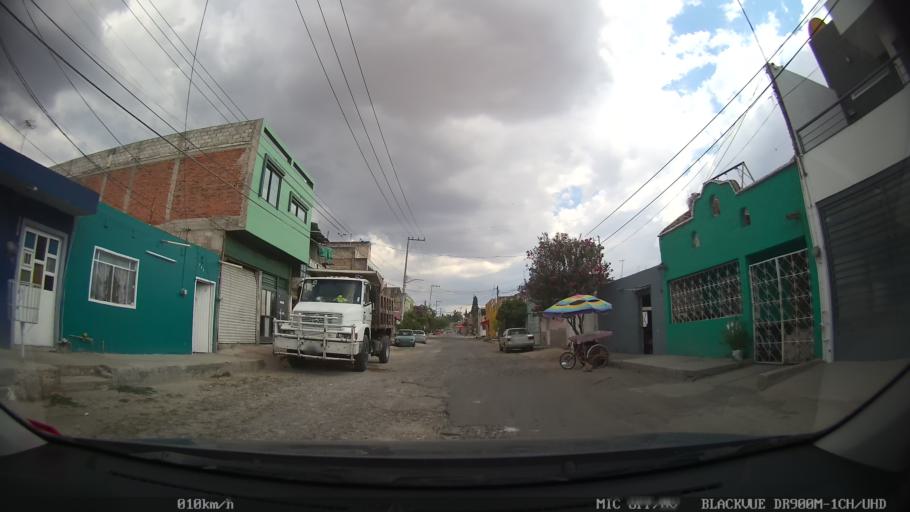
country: MX
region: Jalisco
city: Tlaquepaque
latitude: 20.6858
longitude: -103.2622
